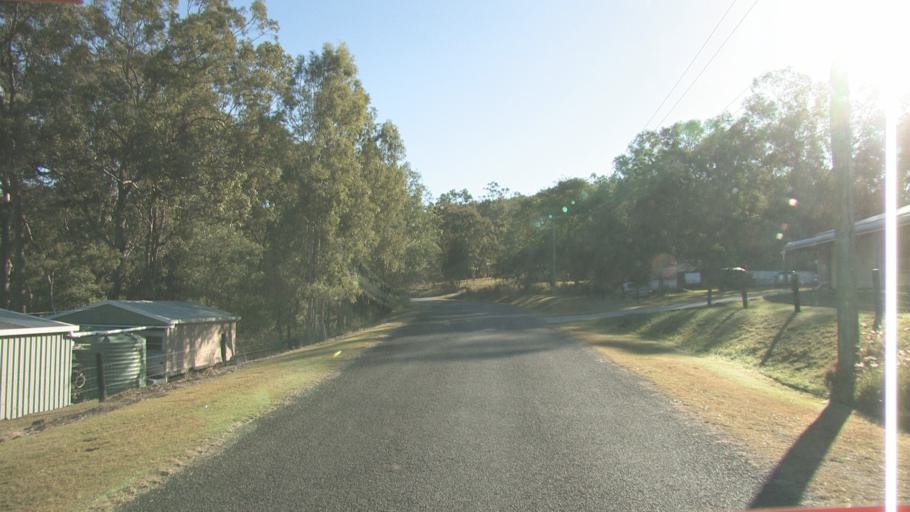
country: AU
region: Queensland
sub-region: Logan
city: Cedar Vale
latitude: -27.8374
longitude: 153.0928
